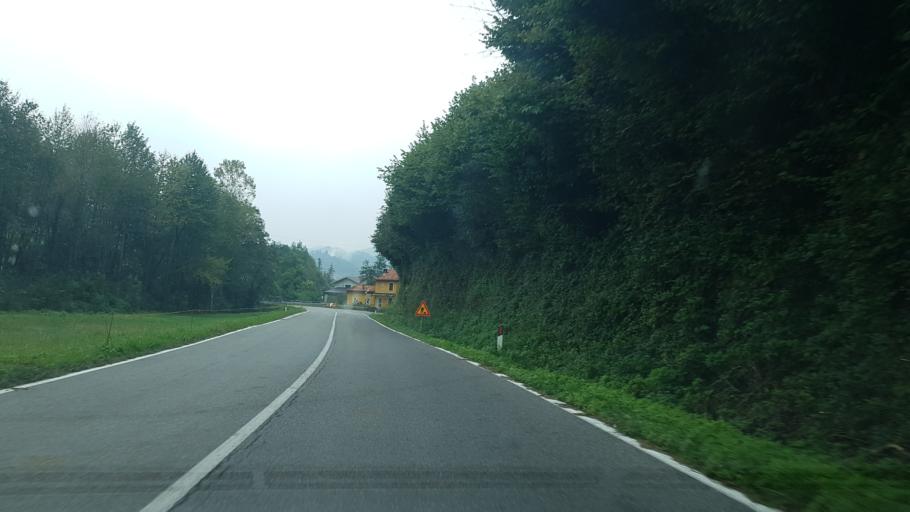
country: IT
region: Piedmont
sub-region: Provincia di Cuneo
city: Villanova Mondovi
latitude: 44.3293
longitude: 7.7876
